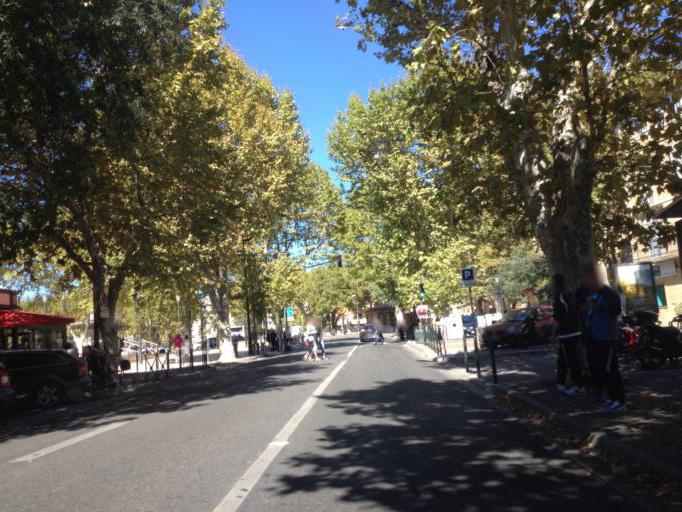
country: FR
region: Provence-Alpes-Cote d'Azur
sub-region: Departement des Bouches-du-Rhone
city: Aix-en-Provence
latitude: 43.5251
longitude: 5.4464
